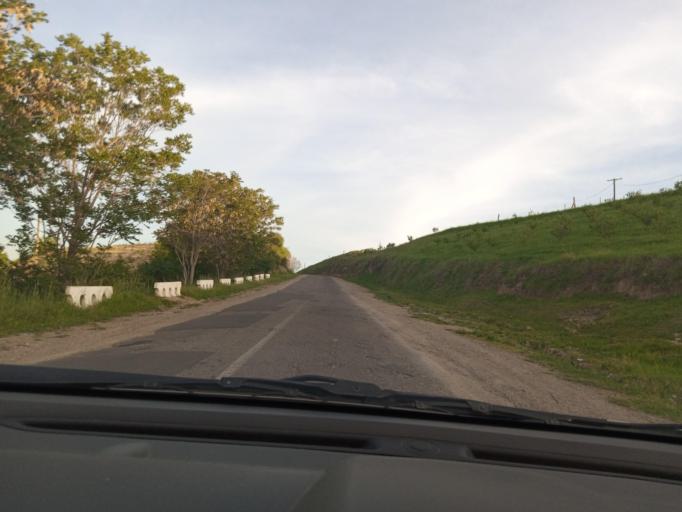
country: UZ
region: Toshkent
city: Parkent
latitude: 41.2406
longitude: 69.7327
